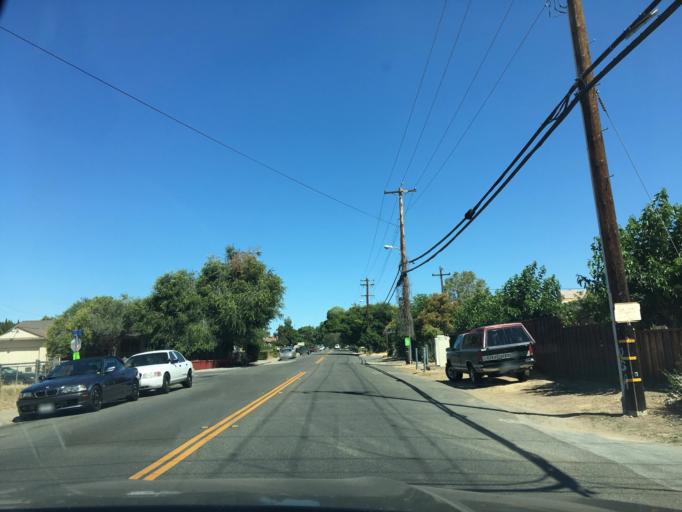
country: US
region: California
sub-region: Santa Clara County
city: East Foothills
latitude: 37.3869
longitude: -121.8303
